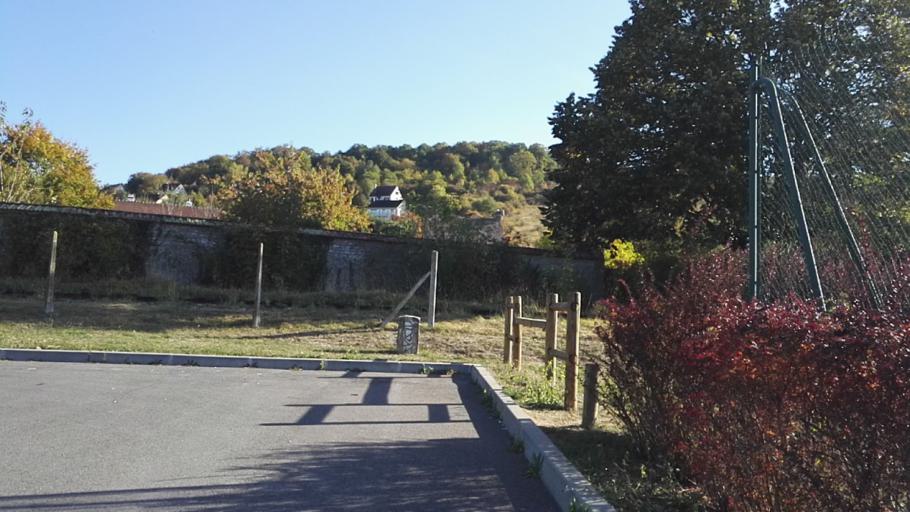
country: FR
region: Haute-Normandie
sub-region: Departement de l'Eure
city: Menilles
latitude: 49.0368
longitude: 1.3613
